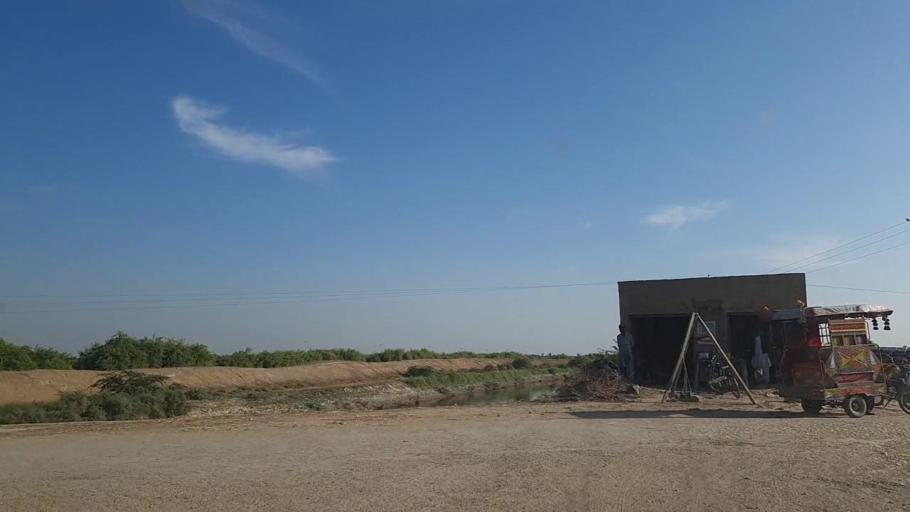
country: PK
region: Sindh
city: Mirpur Batoro
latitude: 24.7407
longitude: 68.3706
